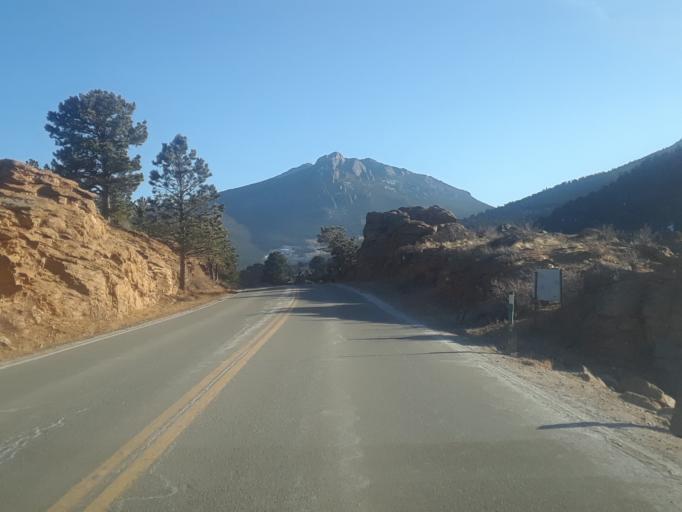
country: US
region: Colorado
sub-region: Larimer County
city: Estes Park
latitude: 40.3455
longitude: -105.5303
